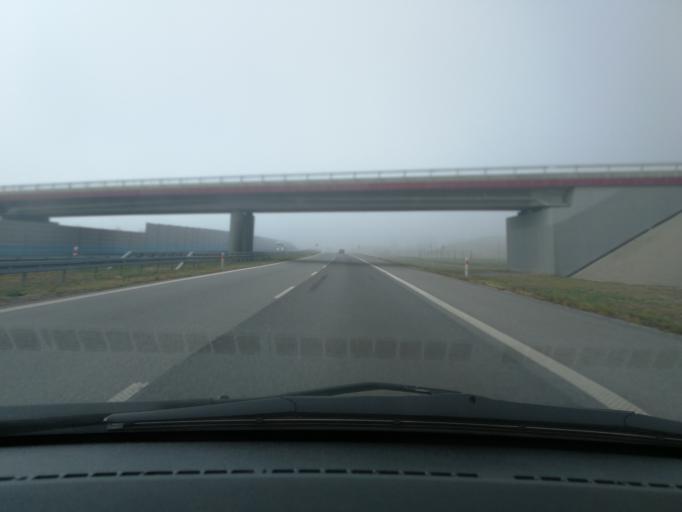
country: PL
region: Lodz Voivodeship
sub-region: powiat Lowicki
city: Lyszkowice
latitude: 52.0136
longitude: 19.9647
